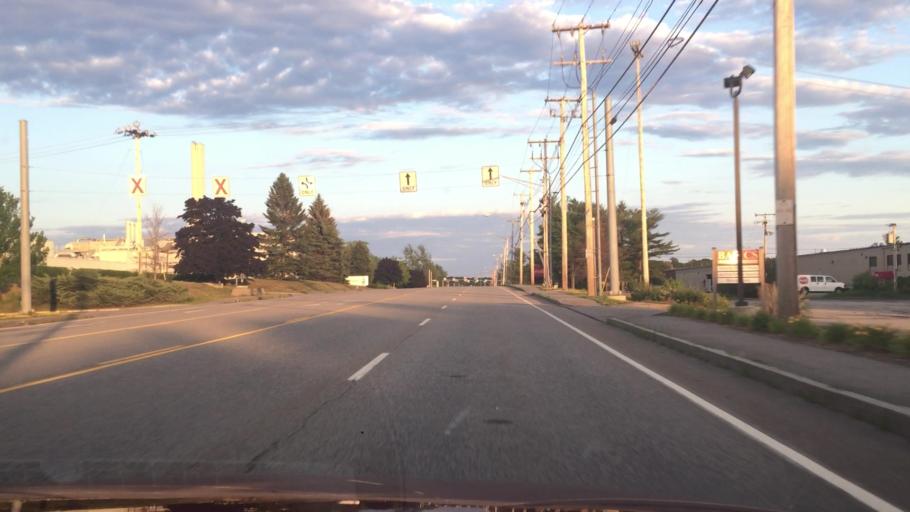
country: US
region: Maine
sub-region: Cumberland County
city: South Portland Gardens
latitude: 43.6415
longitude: -70.3282
